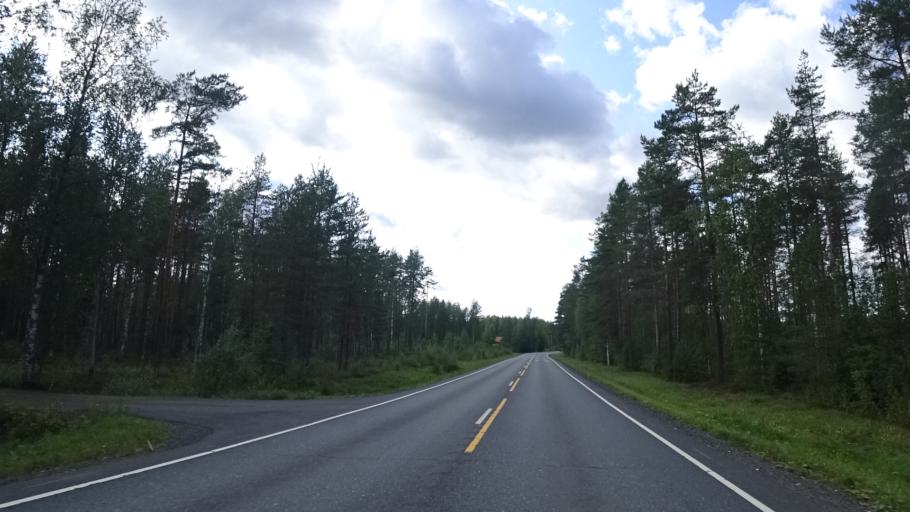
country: RU
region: Republic of Karelia
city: Vyartsilya
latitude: 62.1761
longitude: 30.5401
